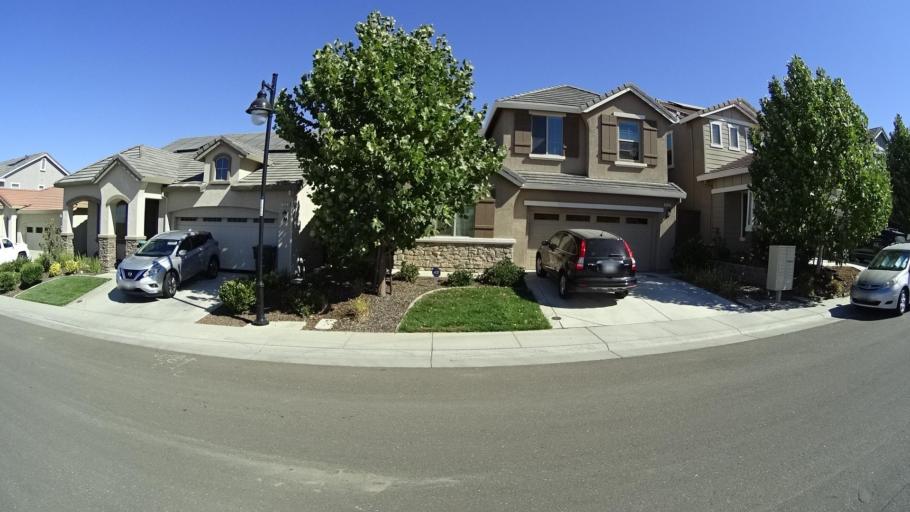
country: US
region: California
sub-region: Placer County
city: Rocklin
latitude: 38.8357
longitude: -121.2675
